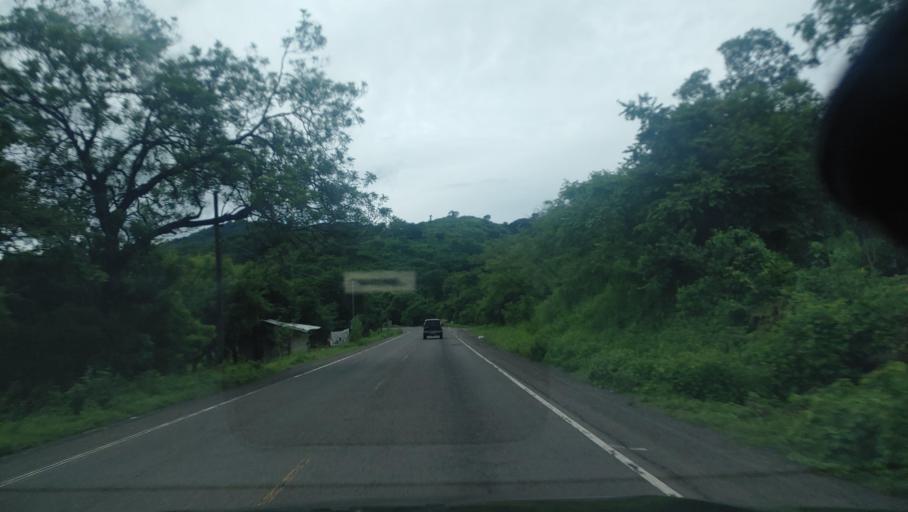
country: HN
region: Choluteca
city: Santa Ana de Yusguare
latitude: 13.3731
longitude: -87.0706
